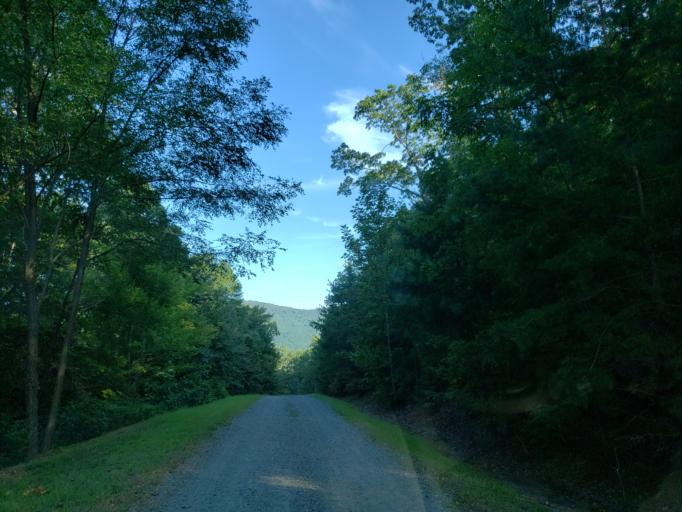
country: US
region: Georgia
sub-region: Fannin County
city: Blue Ridge
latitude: 34.6895
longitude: -84.2769
